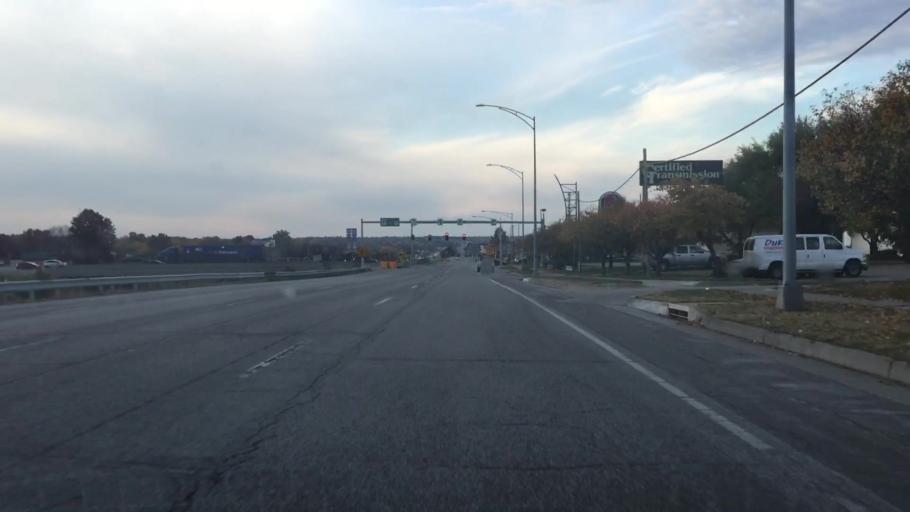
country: US
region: Missouri
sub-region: Jackson County
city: Grandview
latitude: 38.8905
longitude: -94.5256
